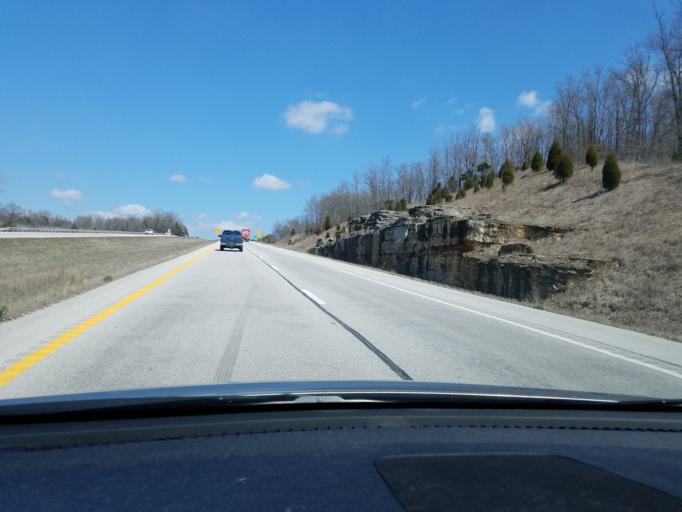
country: US
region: Missouri
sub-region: Taney County
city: Merriam Woods
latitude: 36.8379
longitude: -93.2187
